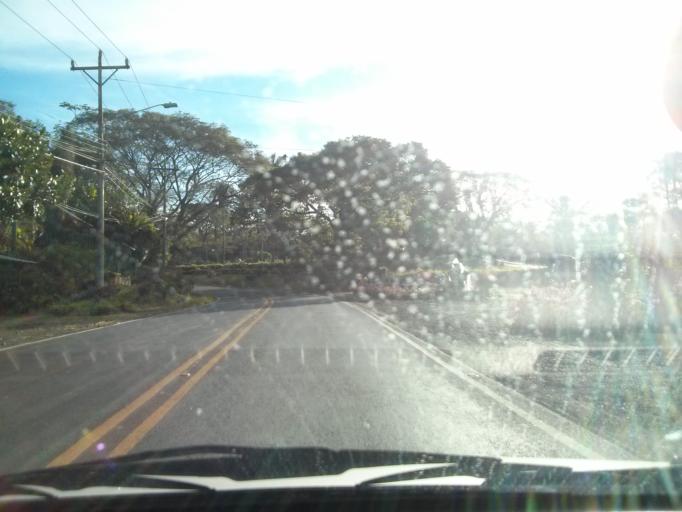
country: CR
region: Alajuela
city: Carrillos
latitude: 10.0061
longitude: -84.2932
